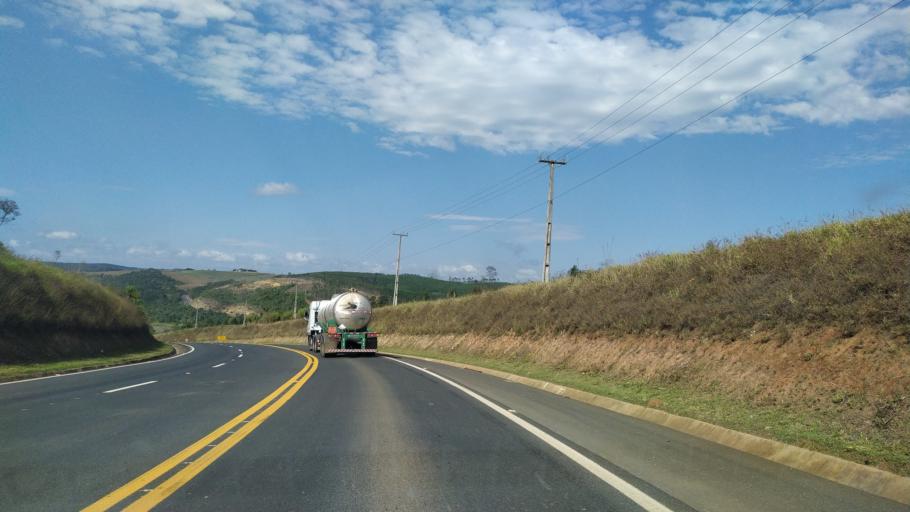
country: BR
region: Parana
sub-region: Telemaco Borba
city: Telemaco Borba
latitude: -24.2582
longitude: -50.7274
